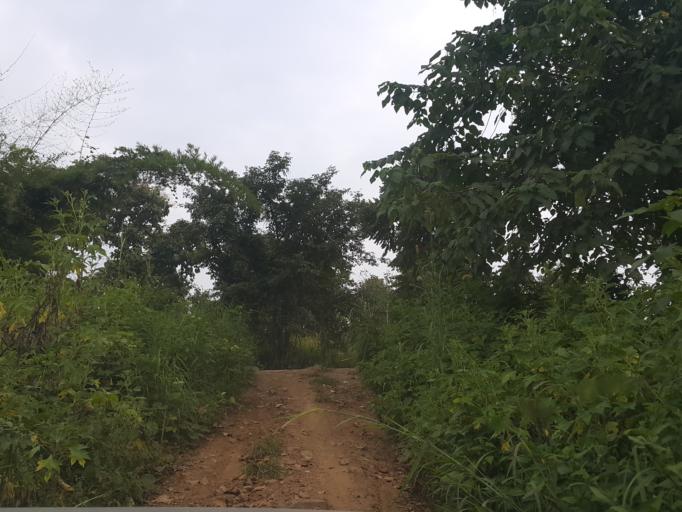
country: TH
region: Mae Hong Son
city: Wiang Nuea
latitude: 19.3843
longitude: 98.4643
